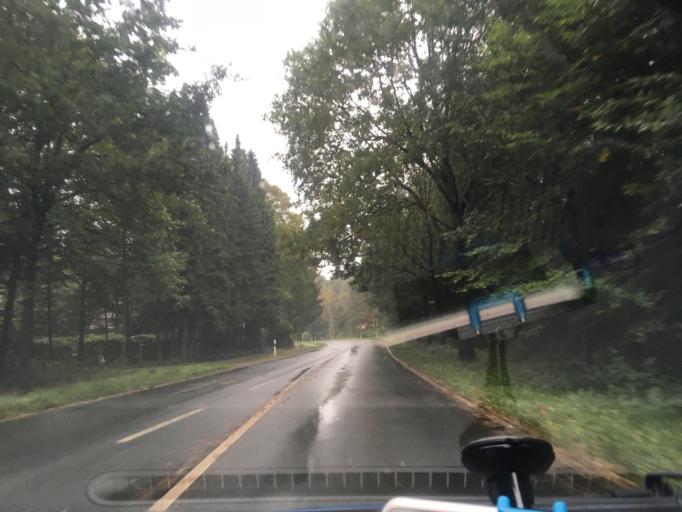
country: DE
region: Lower Saxony
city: Bispingen
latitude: 53.0669
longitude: 9.9954
